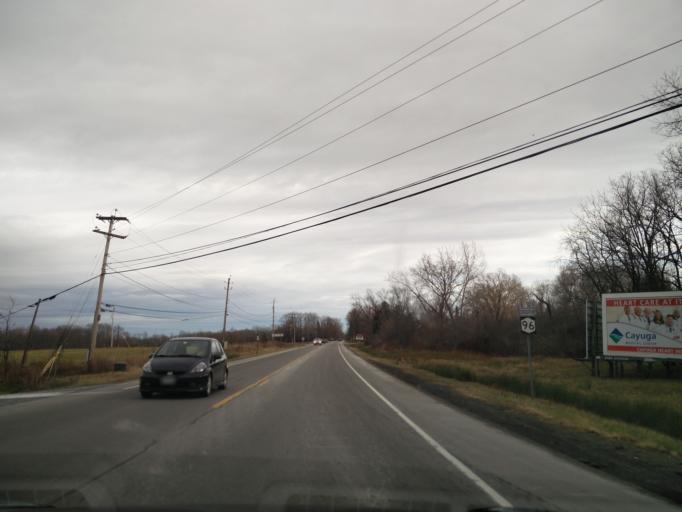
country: US
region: New York
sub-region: Tompkins County
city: Northwest Ithaca
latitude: 42.4959
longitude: -76.5962
